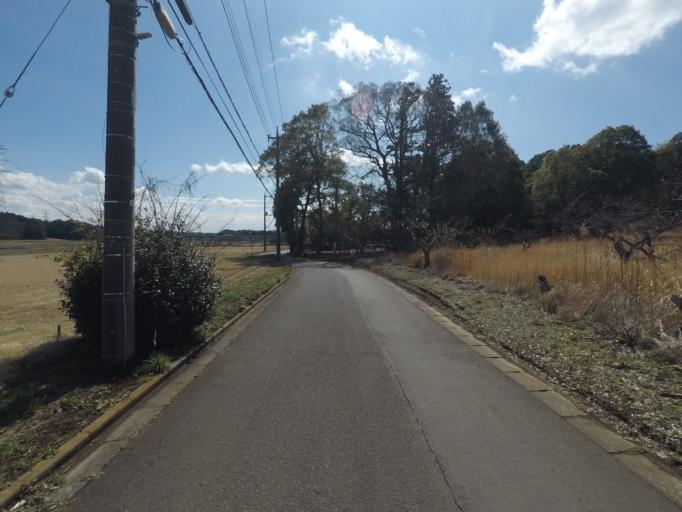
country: JP
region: Ibaraki
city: Mitsukaido
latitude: 36.0248
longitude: 140.0678
